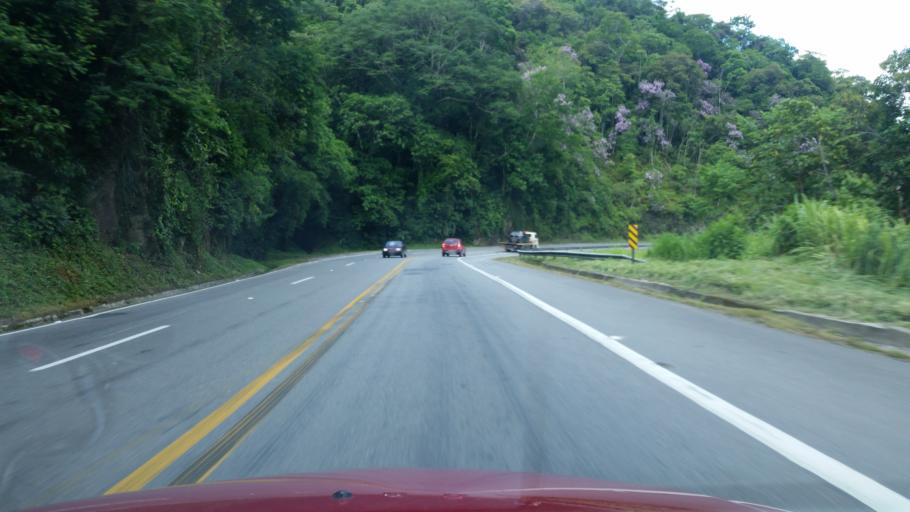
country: BR
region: Sao Paulo
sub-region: Miracatu
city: Miracatu
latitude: -24.2662
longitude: -47.2784
